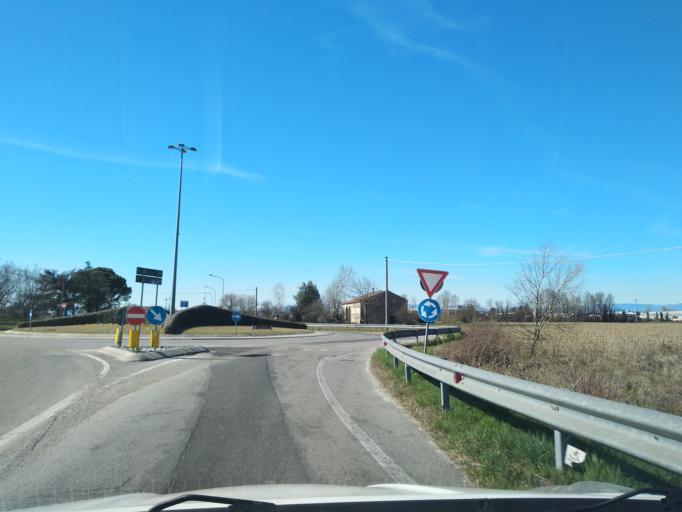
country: IT
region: Veneto
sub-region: Provincia di Padova
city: Caselle
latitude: 45.4136
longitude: 11.8045
